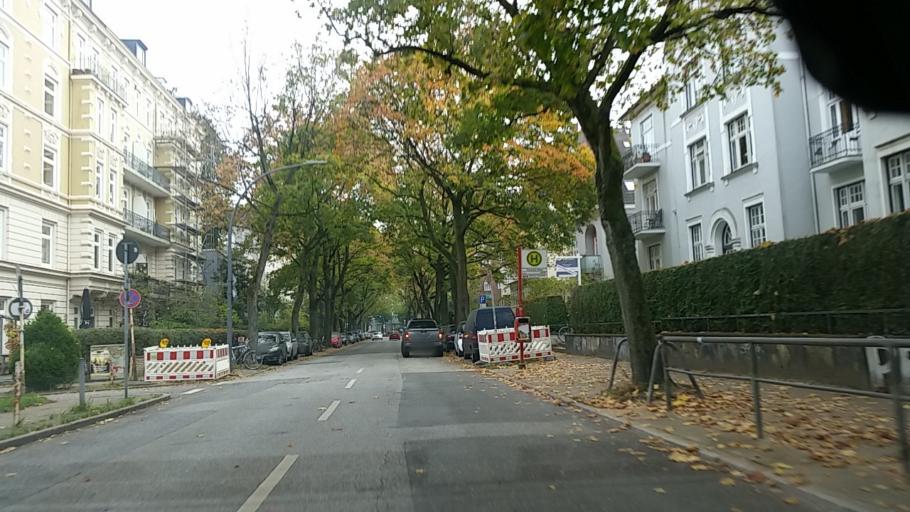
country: DE
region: Hamburg
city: Altona
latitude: 53.5482
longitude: 9.9225
